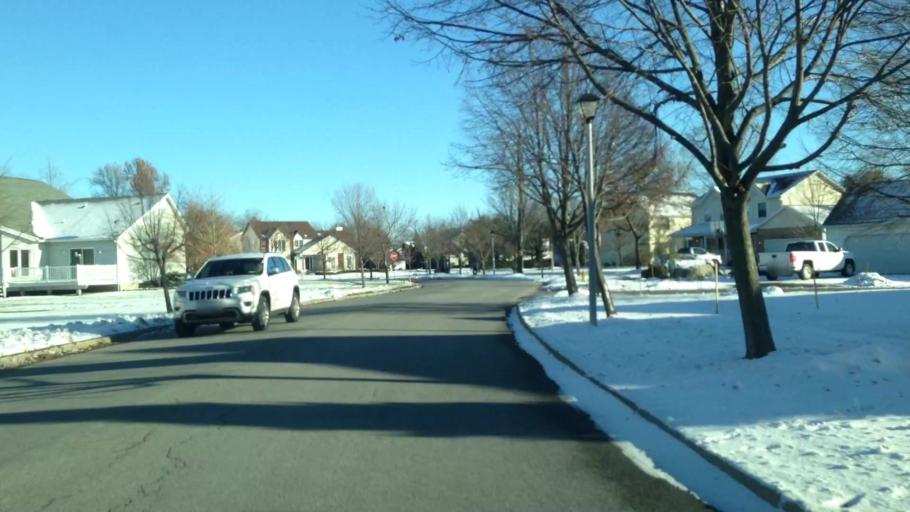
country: US
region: New York
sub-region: Erie County
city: Depew
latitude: 42.8666
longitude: -78.6941
